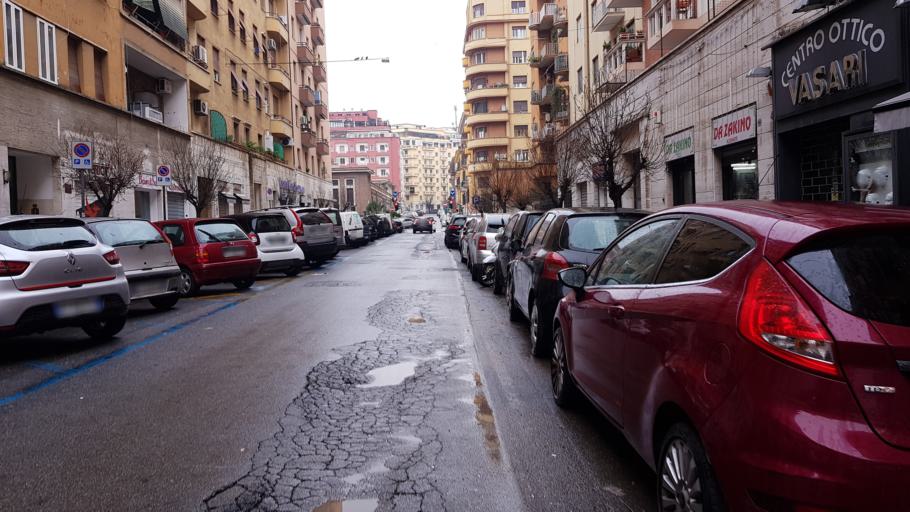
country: IT
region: Latium
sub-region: Citta metropolitana di Roma Capitale
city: Rome
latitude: 41.9107
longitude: 12.5196
